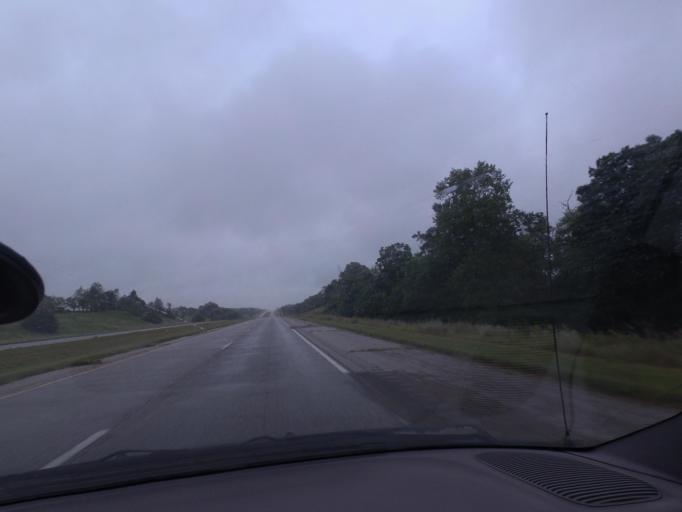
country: US
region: Illinois
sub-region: Pike County
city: Barry
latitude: 39.6927
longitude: -90.9468
